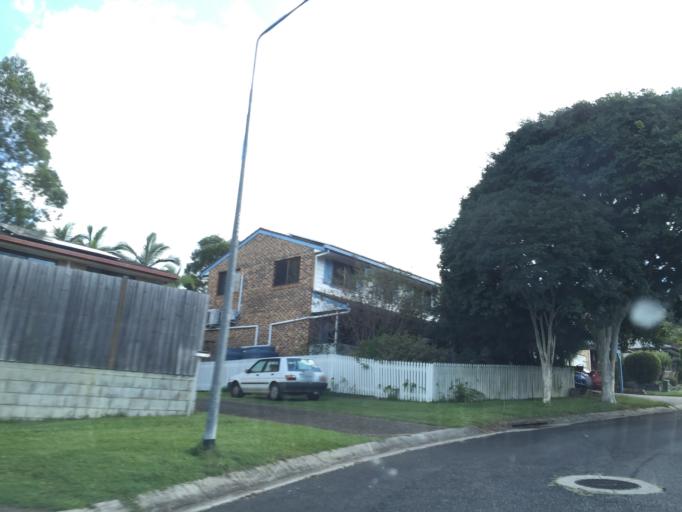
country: AU
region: Queensland
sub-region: Moreton Bay
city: Ferny Hills
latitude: -27.4364
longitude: 152.9299
